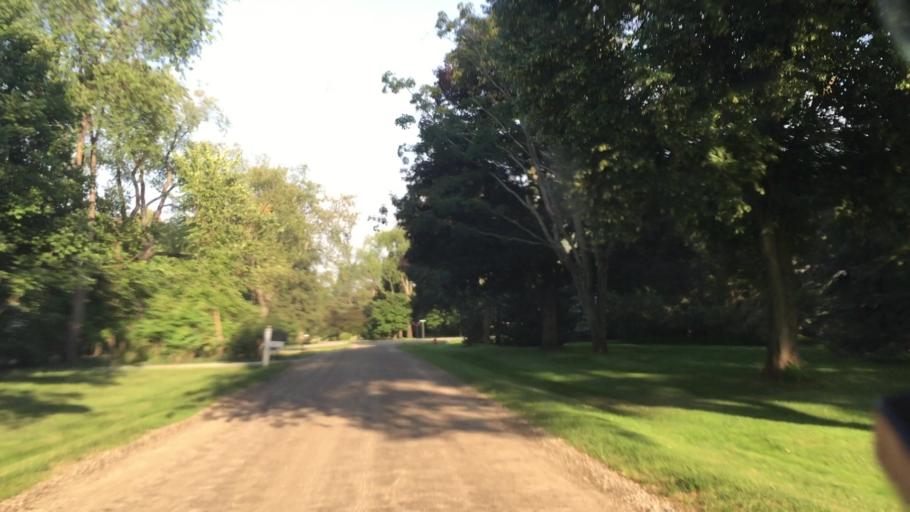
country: US
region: Michigan
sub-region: Oakland County
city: Bloomfield Hills
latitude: 42.5629
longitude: -83.2714
